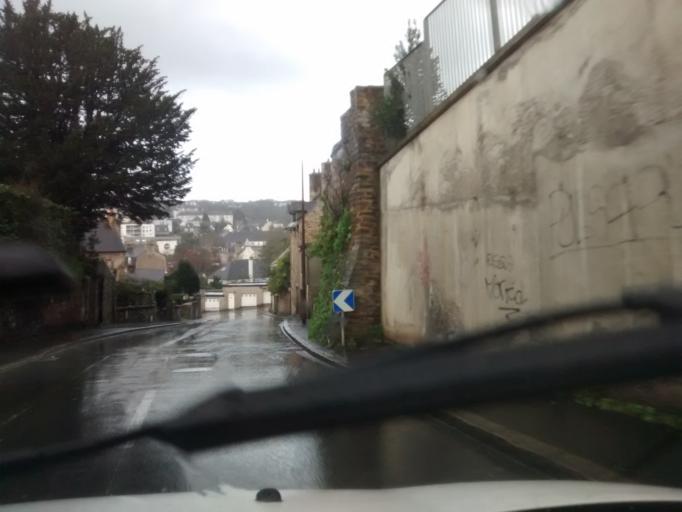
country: FR
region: Brittany
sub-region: Departement des Cotes-d'Armor
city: Lannion
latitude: 48.7289
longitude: -3.4554
